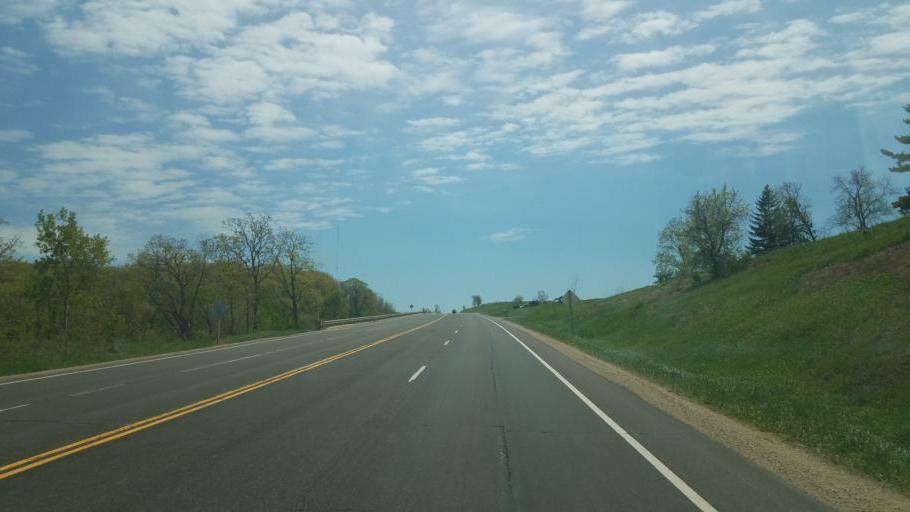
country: US
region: Wisconsin
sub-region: Monroe County
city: Tomah
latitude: 43.9044
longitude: -90.4925
